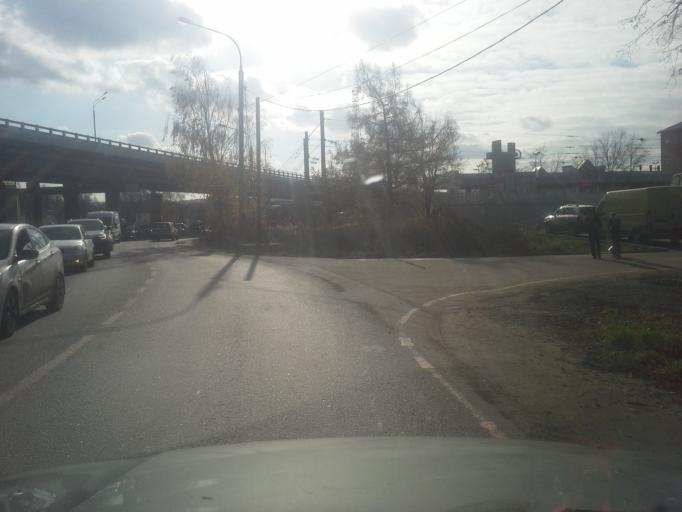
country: RU
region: Moskovskaya
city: Zvenigorod
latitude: 55.7013
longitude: 36.8814
